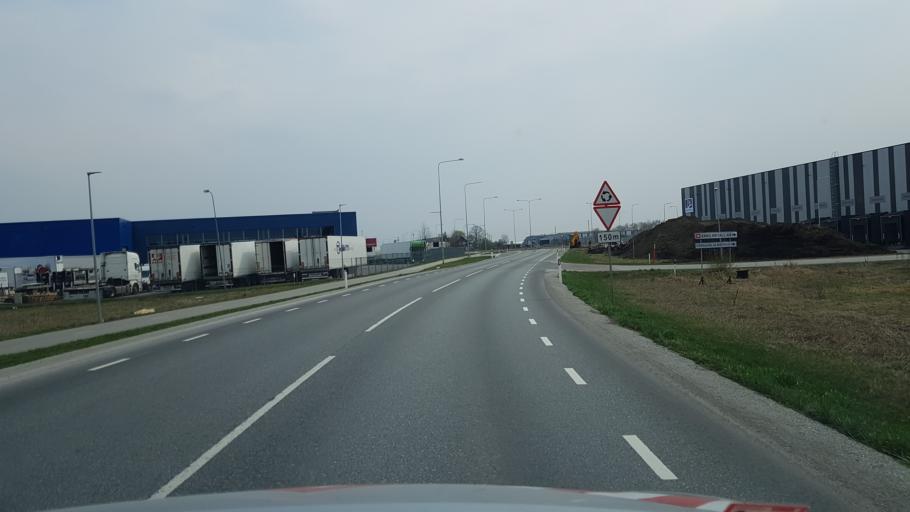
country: EE
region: Harju
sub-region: Rae vald
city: Jueri
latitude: 59.3678
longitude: 24.8699
